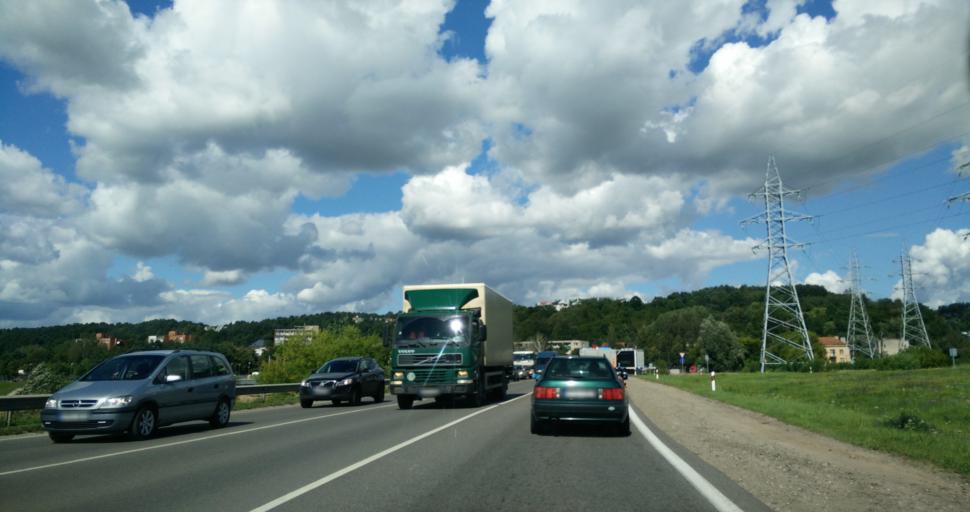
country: LT
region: Kauno apskritis
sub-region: Kauno rajonas
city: Akademija (Kaunas)
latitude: 54.9134
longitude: 23.8337
